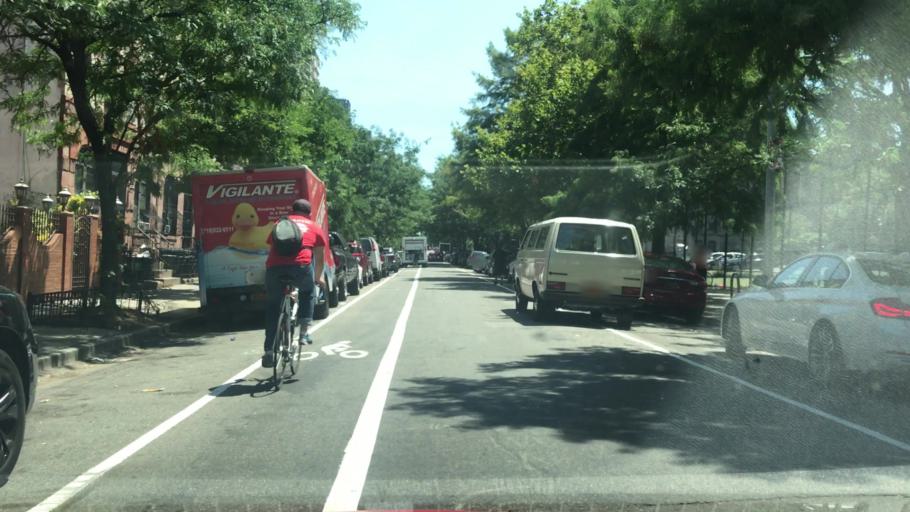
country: US
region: New York
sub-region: Kings County
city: Brooklyn
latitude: 40.6814
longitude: -73.9734
